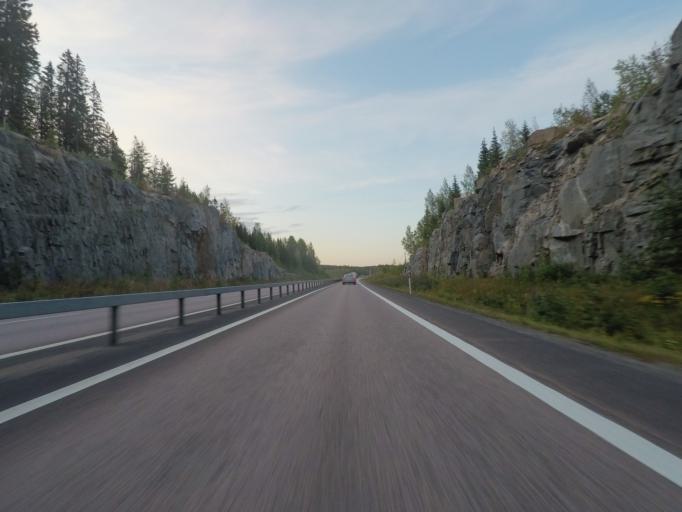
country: FI
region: Central Finland
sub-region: Jyvaeskylae
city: Saeynaetsalo
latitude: 62.2161
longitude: 25.8917
